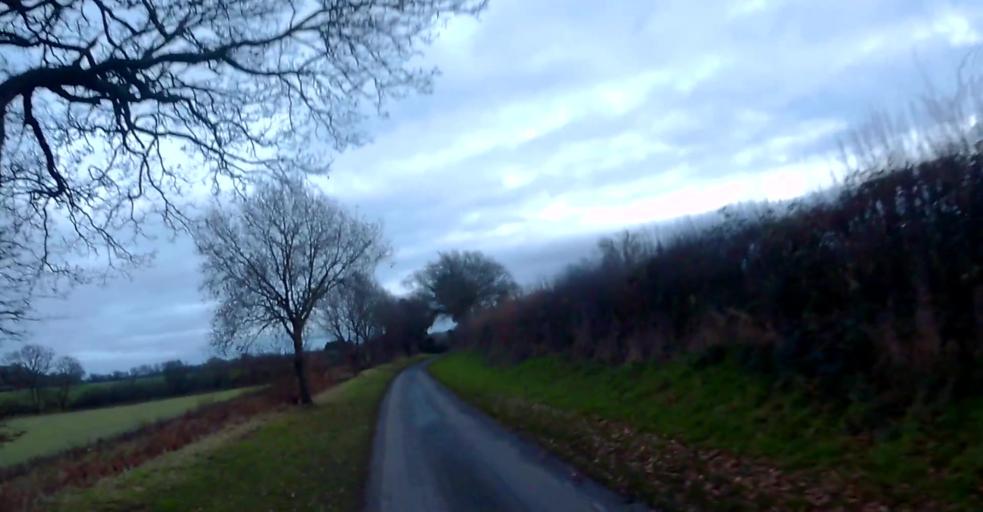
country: GB
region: England
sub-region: Hampshire
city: Overton
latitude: 51.2564
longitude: -1.2134
